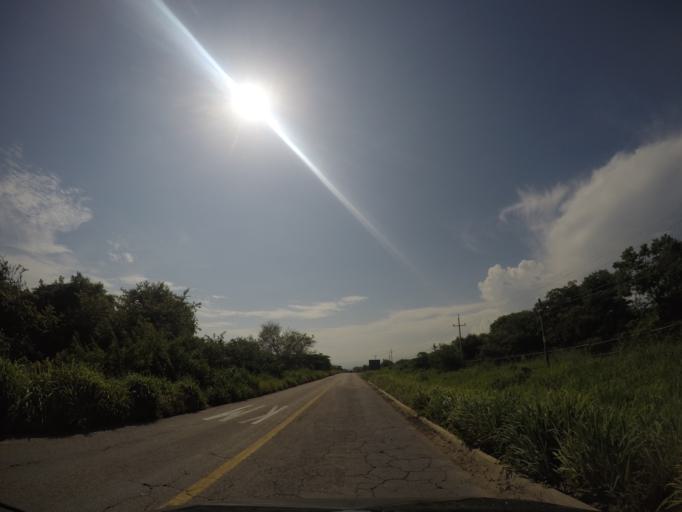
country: MX
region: Oaxaca
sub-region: San Pedro Mixtepec -Dto. 22 -
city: Puerto Escondido
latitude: 15.8746
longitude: -97.0973
